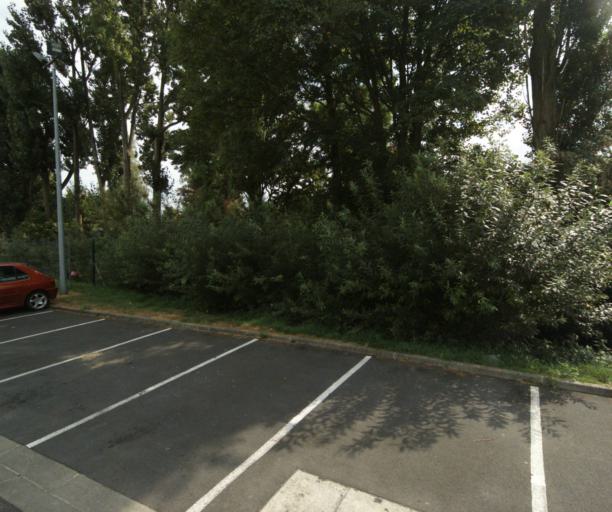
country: FR
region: Nord-Pas-de-Calais
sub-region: Departement du Nord
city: Neuville-en-Ferrain
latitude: 50.7538
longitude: 3.1591
